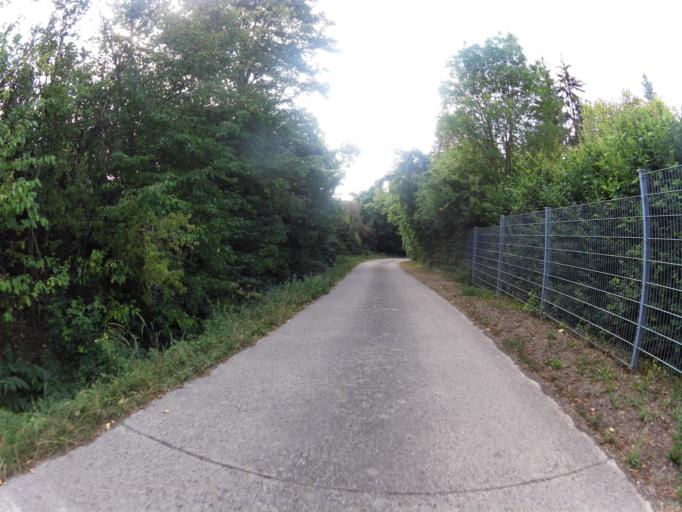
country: DE
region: Bavaria
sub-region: Regierungsbezirk Unterfranken
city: Ochsenfurt
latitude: 49.6512
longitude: 10.0597
